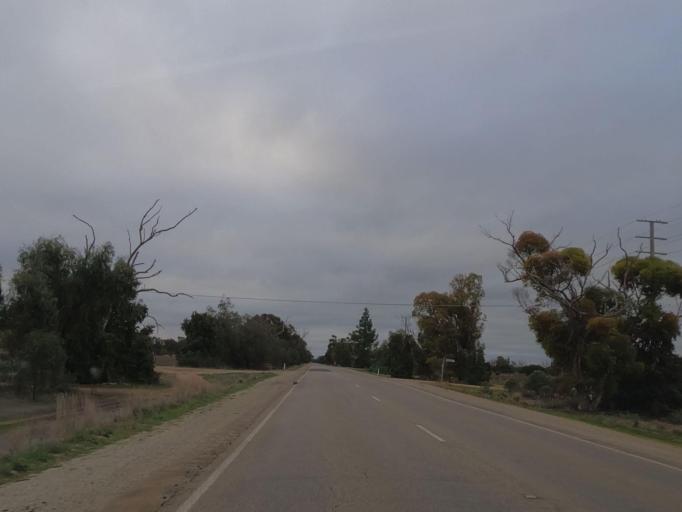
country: AU
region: Victoria
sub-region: Swan Hill
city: Swan Hill
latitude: -35.4305
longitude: 143.6075
